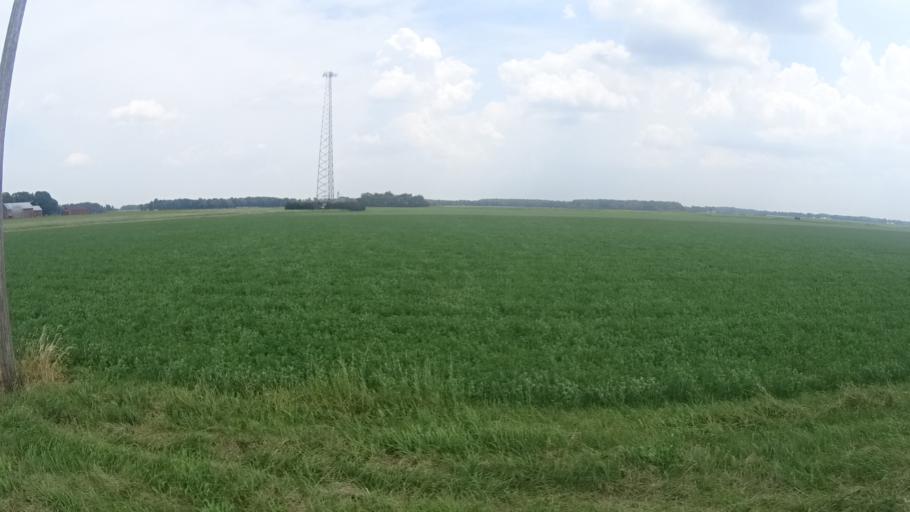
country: US
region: Ohio
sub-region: Huron County
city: Monroeville
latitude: 41.3068
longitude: -82.6926
